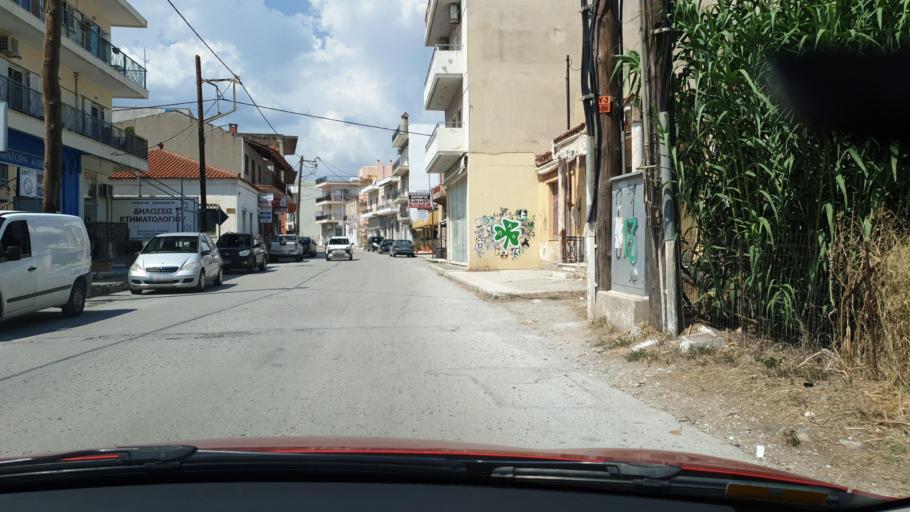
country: GR
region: Central Greece
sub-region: Nomos Evvoias
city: Aliveri
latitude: 38.4079
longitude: 24.0408
